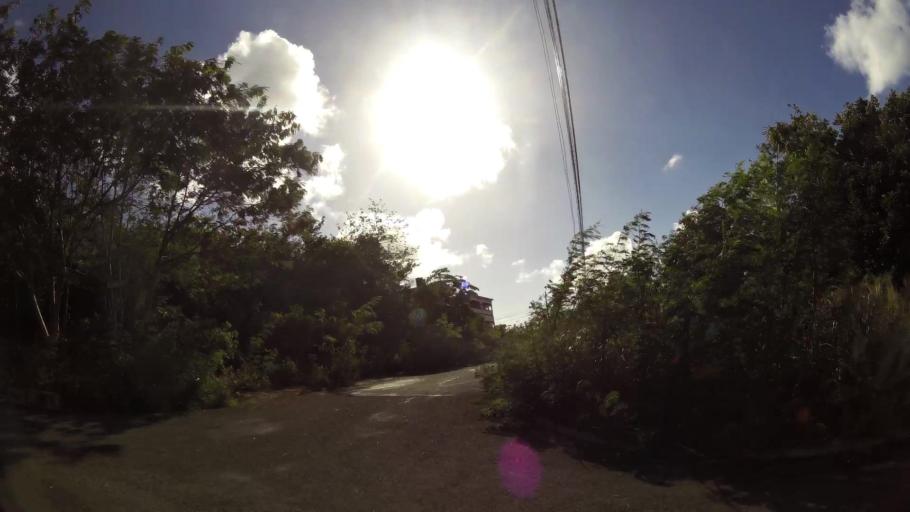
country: LC
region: Castries Quarter
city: Bisee
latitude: 14.0412
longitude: -60.9580
